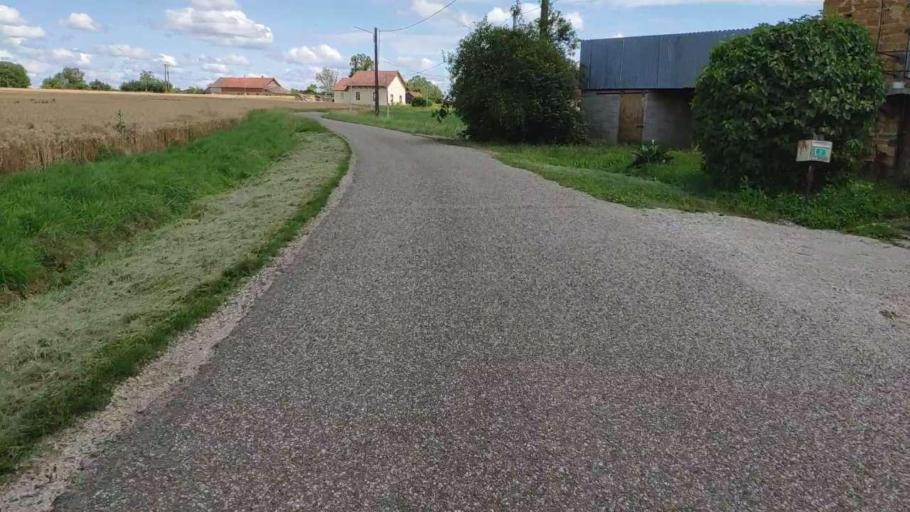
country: FR
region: Franche-Comte
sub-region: Departement du Jura
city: Chaussin
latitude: 46.8867
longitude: 5.4877
